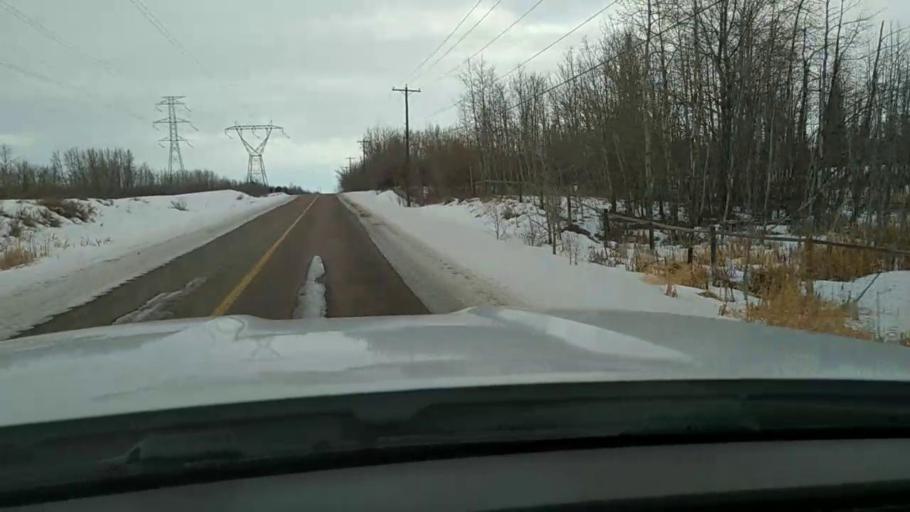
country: CA
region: Alberta
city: Cochrane
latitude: 51.1787
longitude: -114.2575
